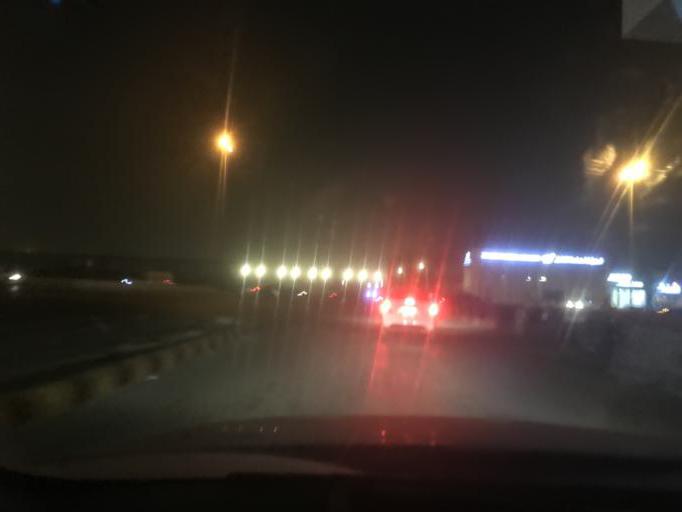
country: SA
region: Ar Riyad
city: Riyadh
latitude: 24.8325
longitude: 46.7333
